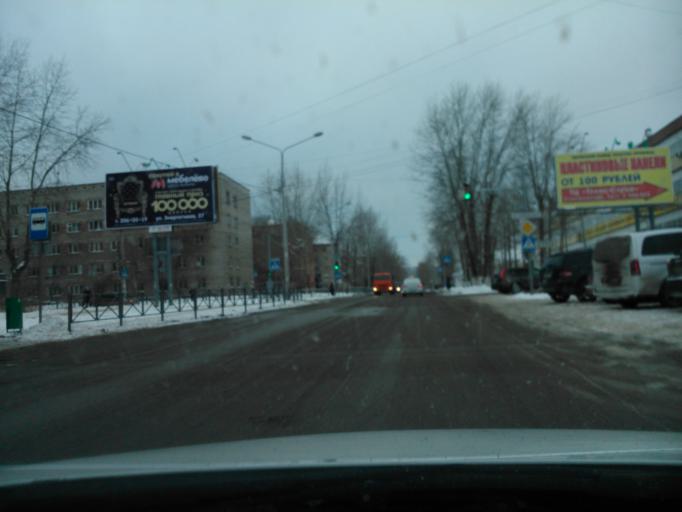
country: RU
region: Perm
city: Perm
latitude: 57.9877
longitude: 56.2072
